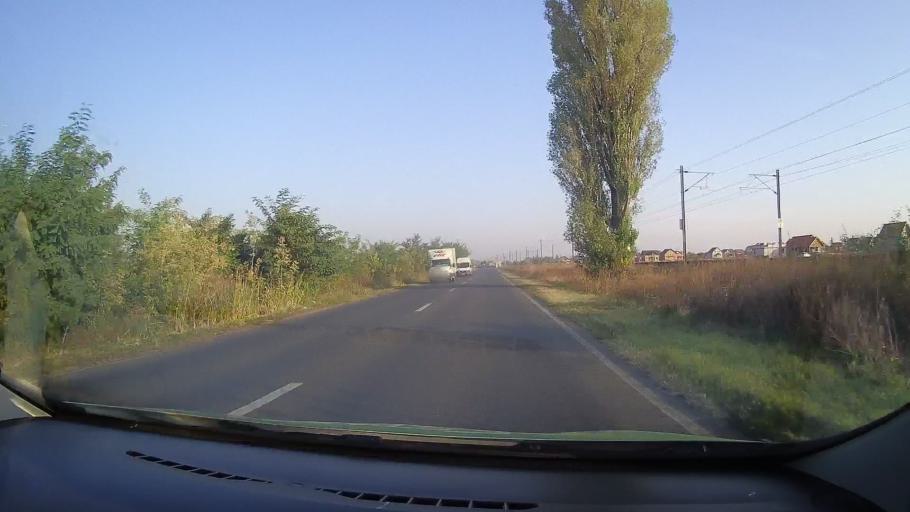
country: RO
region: Arad
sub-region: Comuna Curtici
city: Curtici
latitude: 46.3256
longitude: 21.3058
